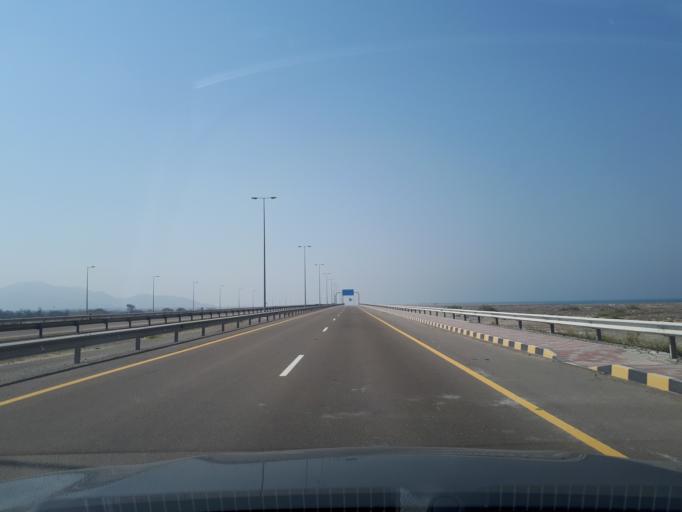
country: AE
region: Al Fujayrah
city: Al Fujayrah
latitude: 24.9402
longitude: 56.3823
